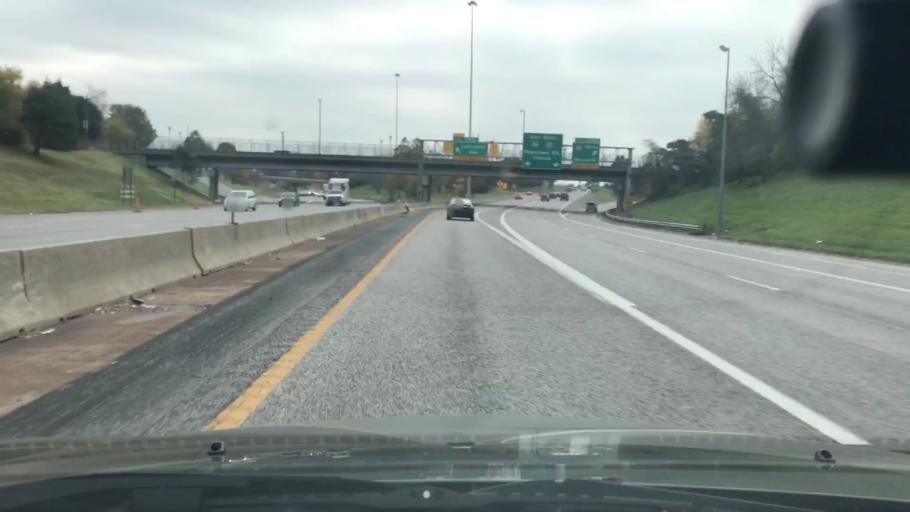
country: US
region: Missouri
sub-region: City of Saint Louis
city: St. Louis
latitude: 38.6126
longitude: -90.2161
